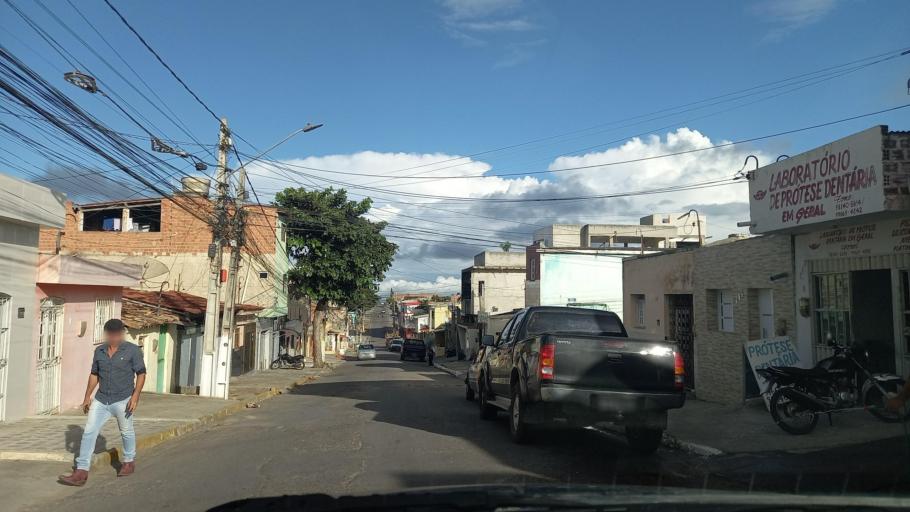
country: BR
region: Pernambuco
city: Garanhuns
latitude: -8.8998
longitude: -36.4946
